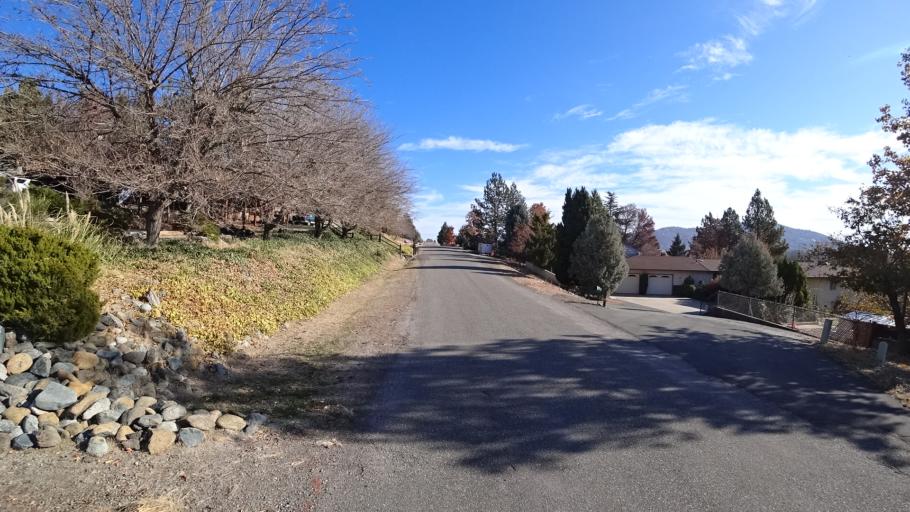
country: US
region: California
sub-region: Siskiyou County
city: Yreka
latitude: 41.6929
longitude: -122.6540
